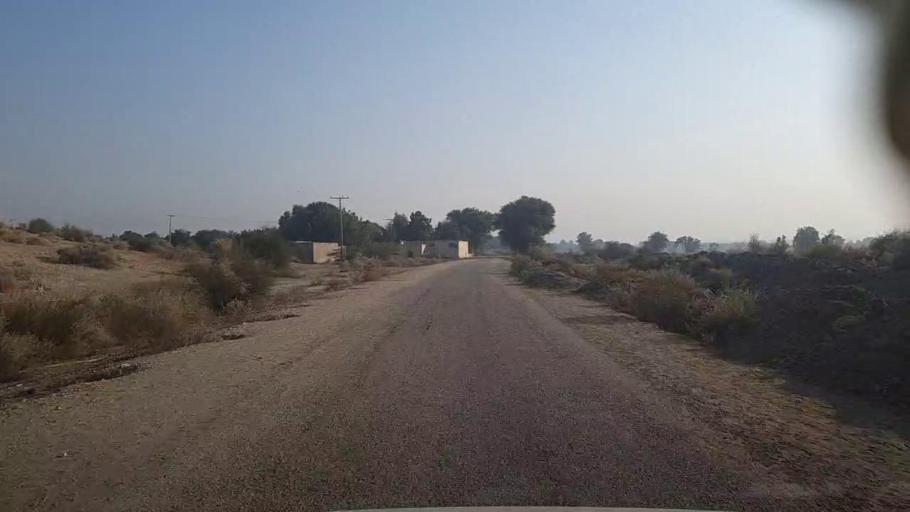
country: PK
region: Sindh
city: Karaundi
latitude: 26.7618
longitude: 68.4756
